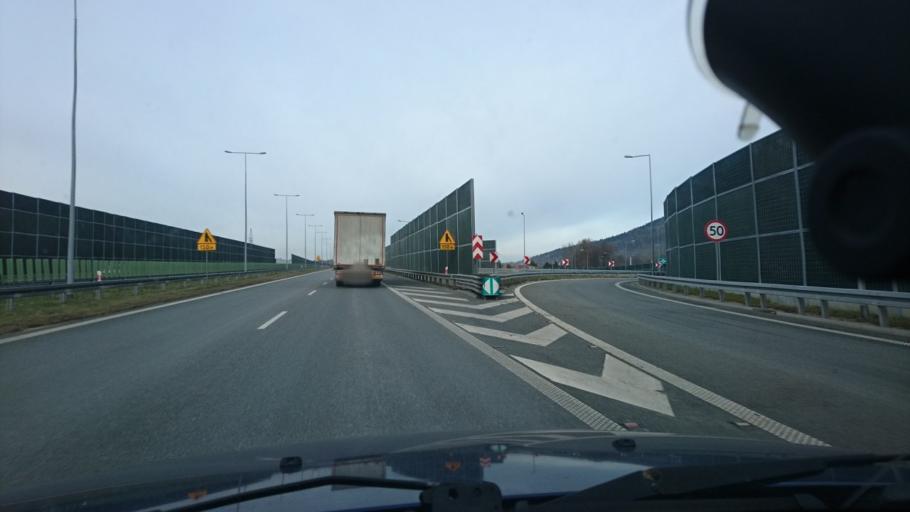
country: PL
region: Silesian Voivodeship
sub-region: Powiat bielski
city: Wilkowice
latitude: 49.7611
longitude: 19.0846
